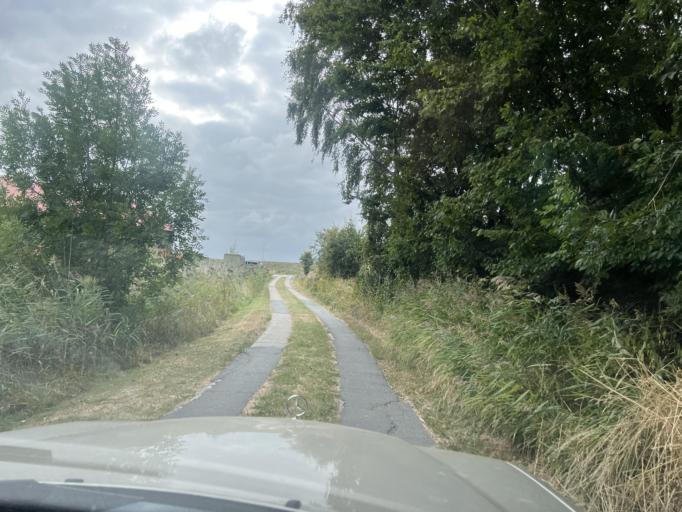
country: DE
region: Schleswig-Holstein
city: Lehe
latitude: 54.3327
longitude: 8.9967
